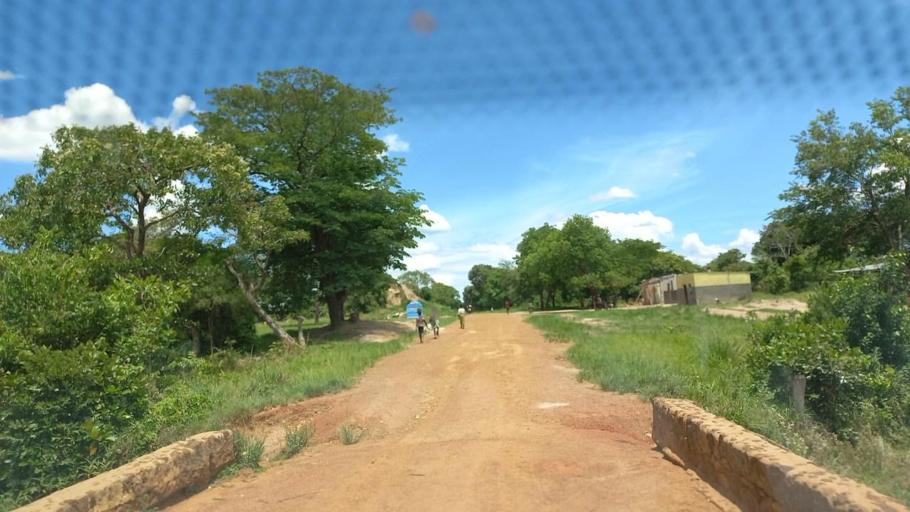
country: ZM
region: North-Western
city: Kabompo
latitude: -12.7472
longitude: 24.2667
